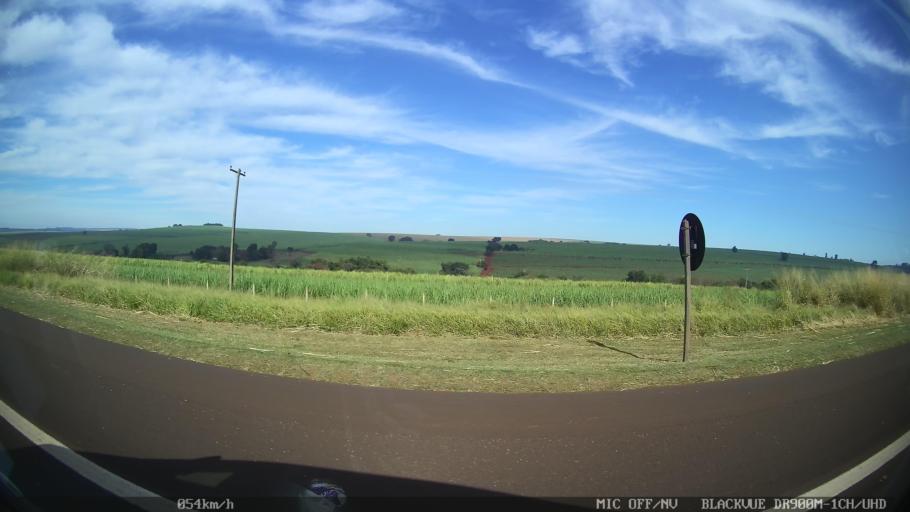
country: BR
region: Sao Paulo
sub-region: Americo Brasiliense
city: Americo Brasiliense
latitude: -21.7639
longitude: -48.0816
